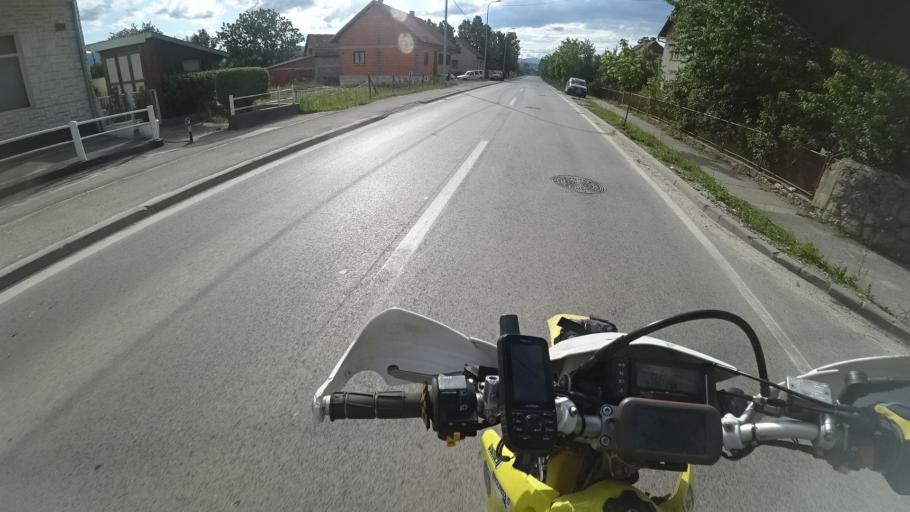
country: HR
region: Licko-Senjska
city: Gospic
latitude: 44.5356
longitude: 15.3933
